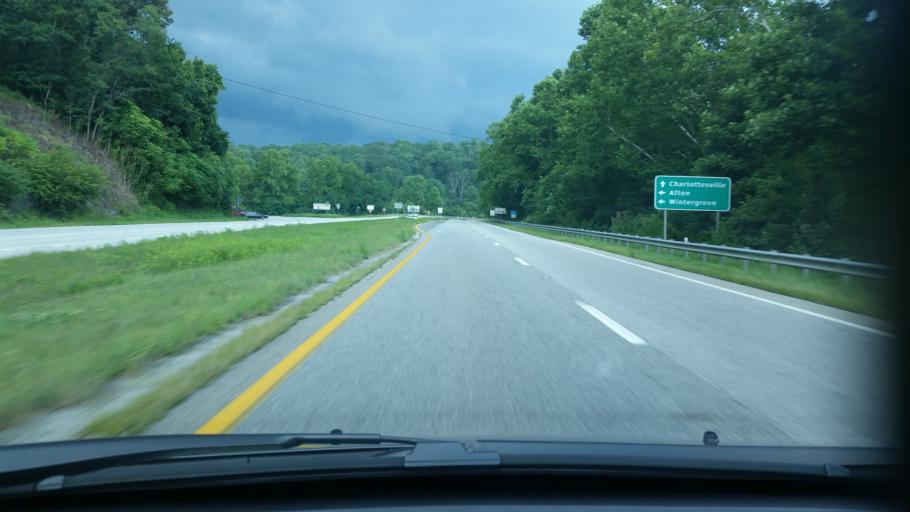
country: US
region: Virginia
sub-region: Nelson County
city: Nellysford
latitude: 37.8440
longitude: -78.8235
